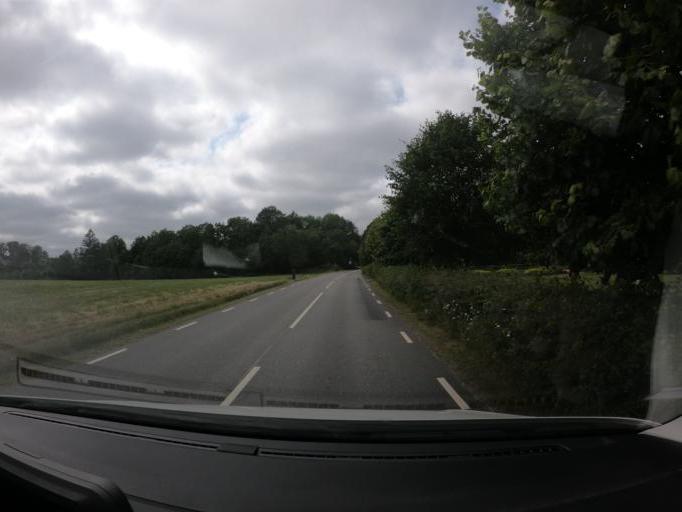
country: SE
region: Skane
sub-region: Hassleholms Kommun
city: Tormestorp
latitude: 56.1564
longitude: 13.6309
